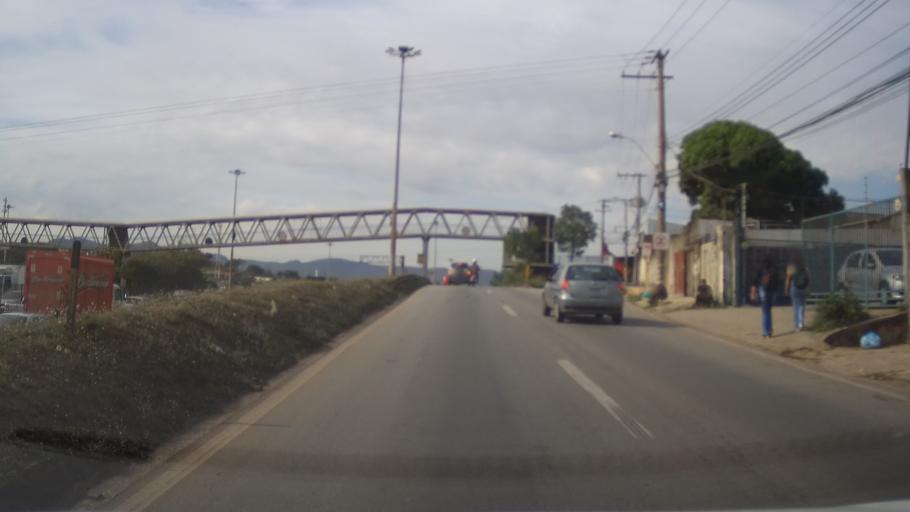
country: BR
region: Minas Gerais
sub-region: Contagem
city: Contagem
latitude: -19.9440
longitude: -44.0082
